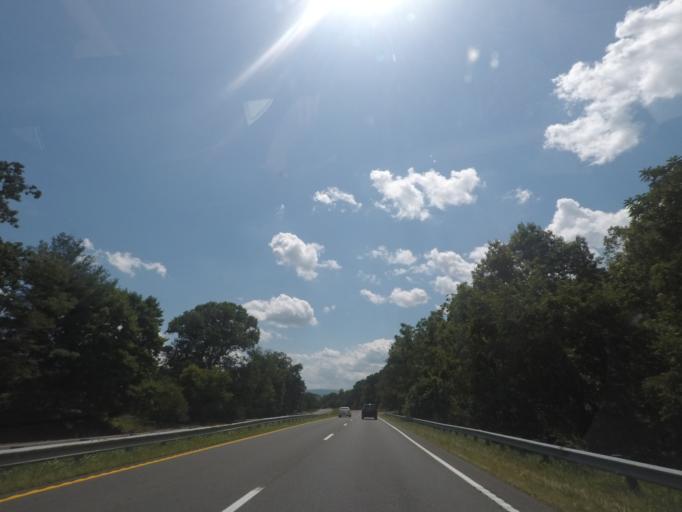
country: US
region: Virginia
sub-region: City of Winchester
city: Winchester
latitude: 39.1021
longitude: -78.1132
